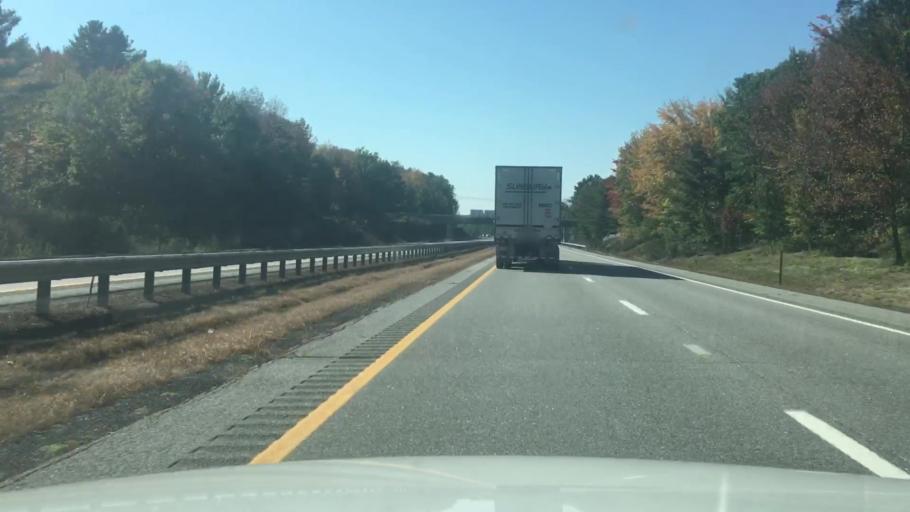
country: US
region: Maine
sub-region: Cumberland County
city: Falmouth
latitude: 43.7306
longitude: -70.2739
